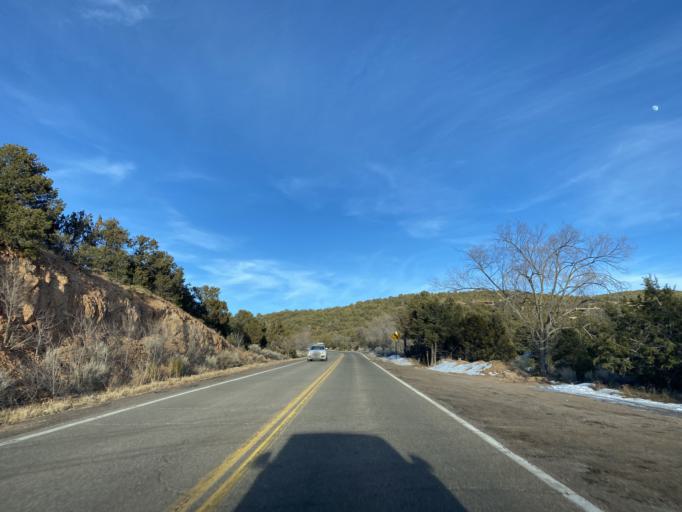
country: US
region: New Mexico
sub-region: Santa Fe County
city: Santa Fe
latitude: 35.7060
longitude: -105.9022
